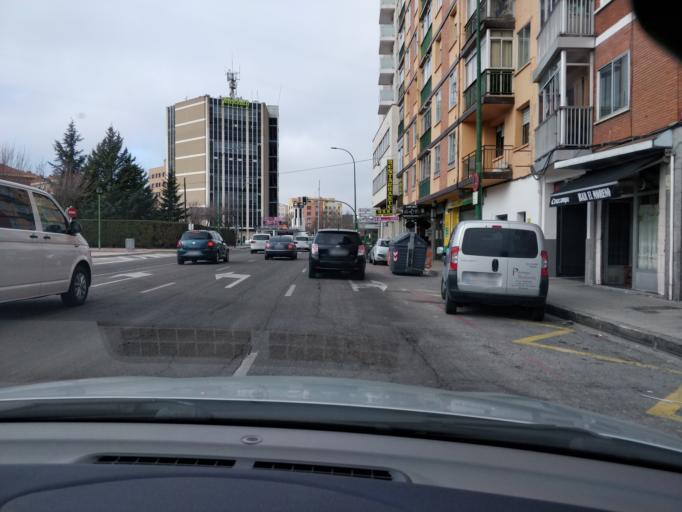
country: ES
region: Castille and Leon
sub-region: Provincia de Burgos
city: Burgos
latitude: 42.3486
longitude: -3.6760
